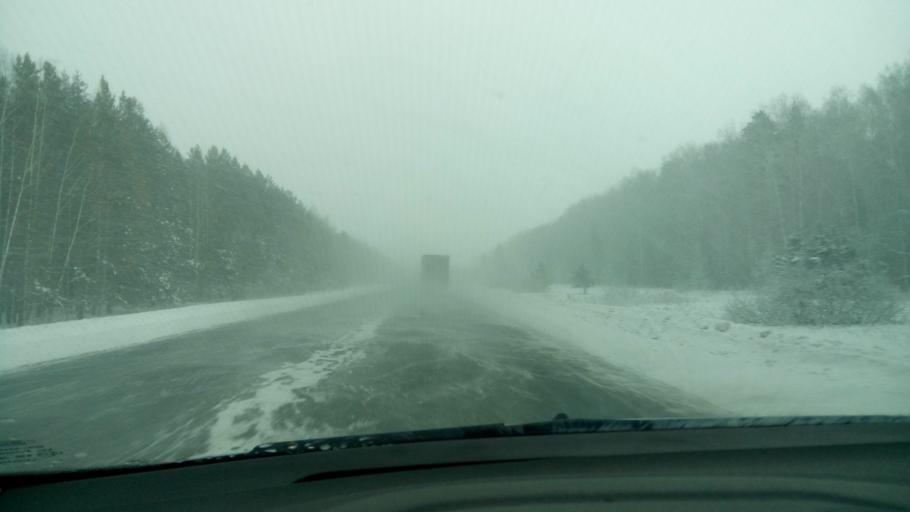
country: RU
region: Sverdlovsk
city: Gryaznovskoye
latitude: 56.7783
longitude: 61.5749
